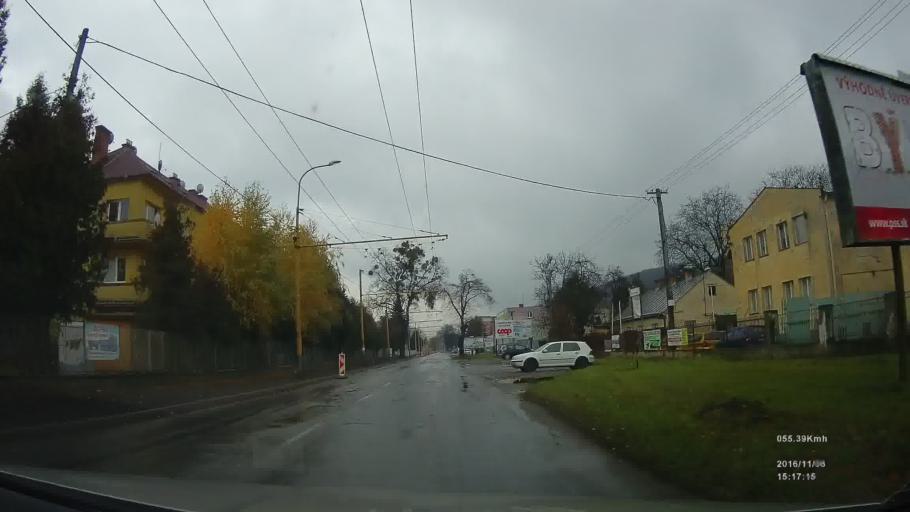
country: SK
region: Presovsky
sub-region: Okres Presov
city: Presov
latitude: 48.9815
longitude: 21.2437
